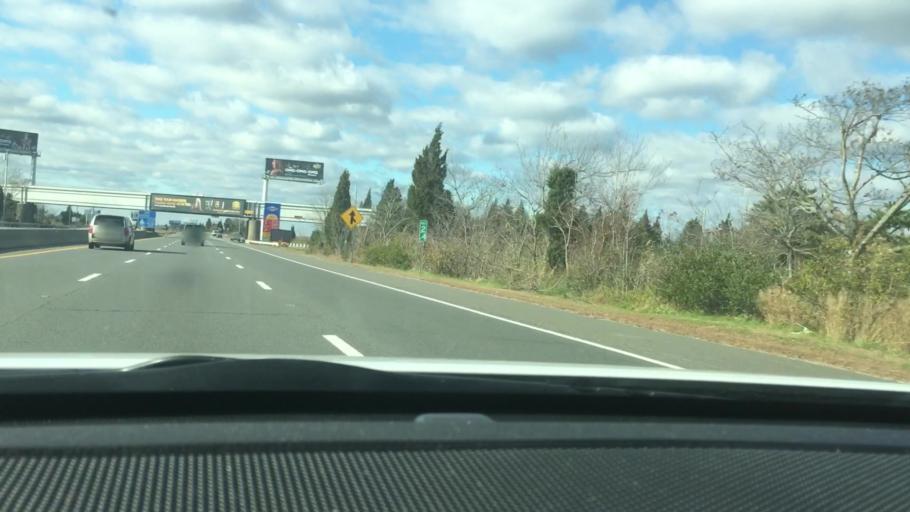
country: US
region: New Jersey
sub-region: Atlantic County
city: Ventnor City
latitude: 39.3766
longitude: -74.4803
